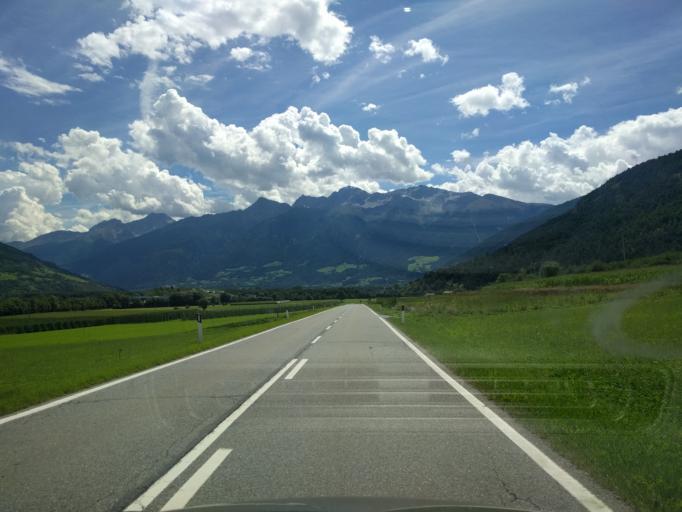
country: IT
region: Trentino-Alto Adige
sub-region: Bolzano
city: Glorenza
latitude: 46.6644
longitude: 10.5581
